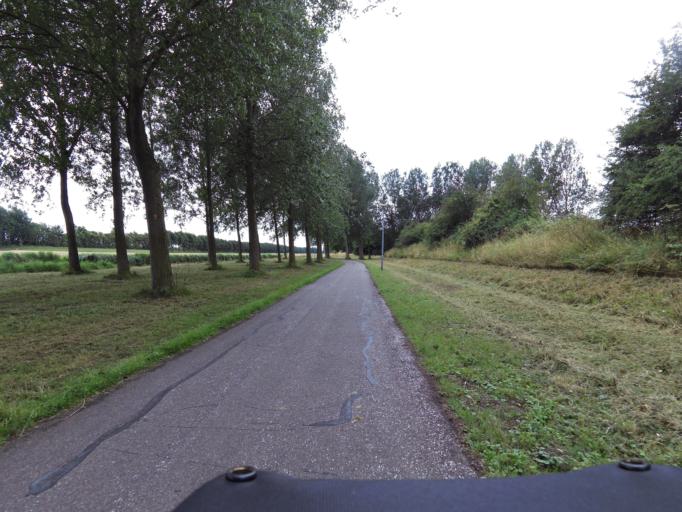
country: NL
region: South Holland
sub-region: Gemeente Goeree-Overflakkee
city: Goedereede
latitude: 51.8278
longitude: 4.0037
